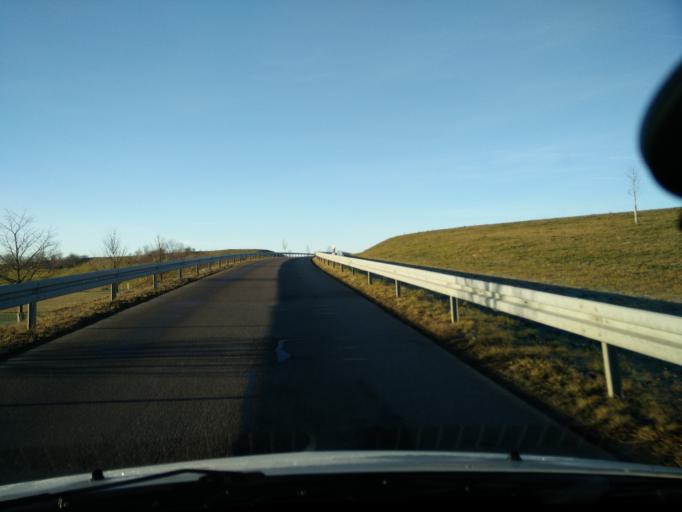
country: DE
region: Bavaria
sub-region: Upper Bavaria
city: Germering
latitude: 48.1503
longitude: 11.3965
